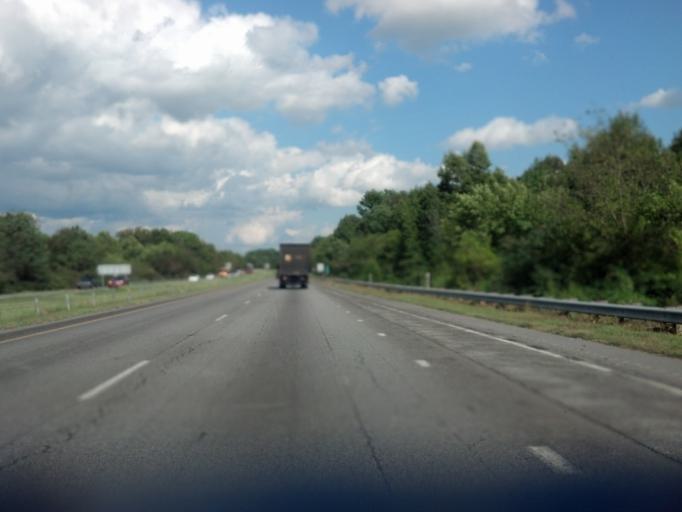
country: US
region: North Carolina
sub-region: Nash County
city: Rocky Mount
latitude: 35.9581
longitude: -77.7792
